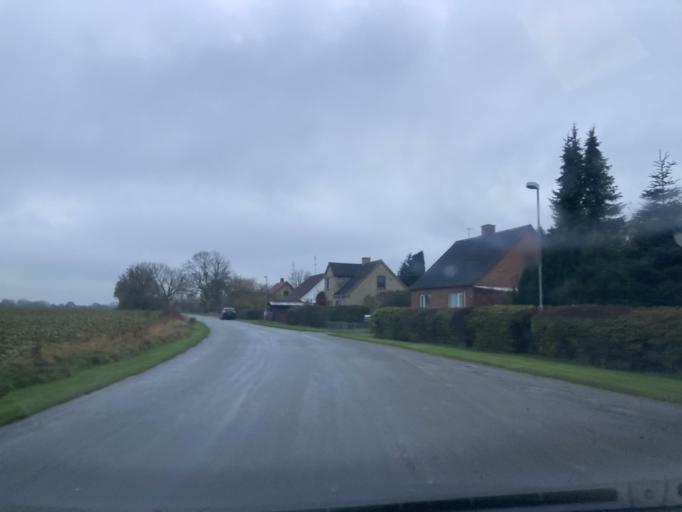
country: DK
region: Zealand
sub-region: Lolland Kommune
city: Holeby
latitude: 54.6770
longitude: 11.4463
